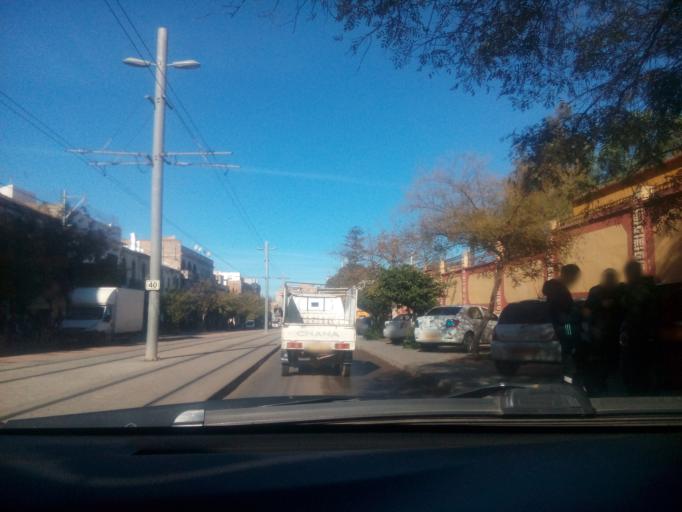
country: DZ
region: Oran
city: Oran
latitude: 35.6949
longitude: -0.6508
